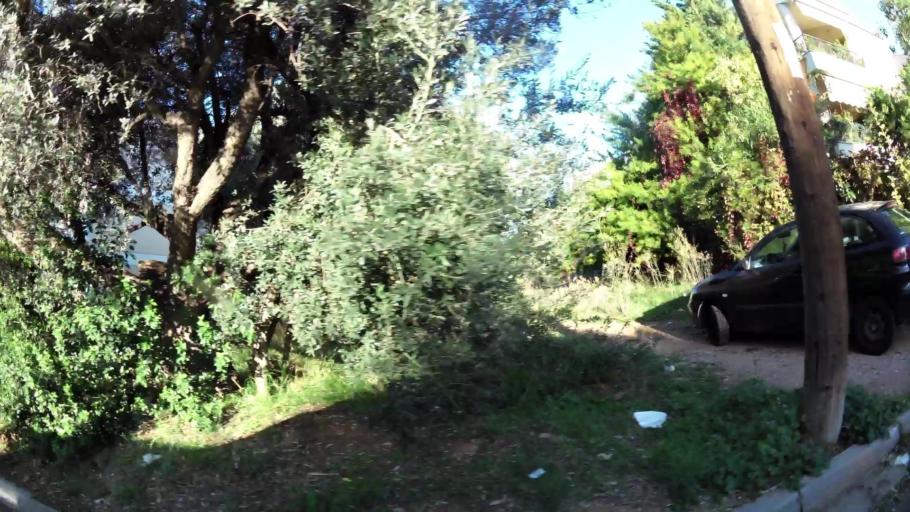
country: GR
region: Attica
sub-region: Nomarchia Athinas
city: Vrilissia
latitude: 38.0314
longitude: 23.8435
